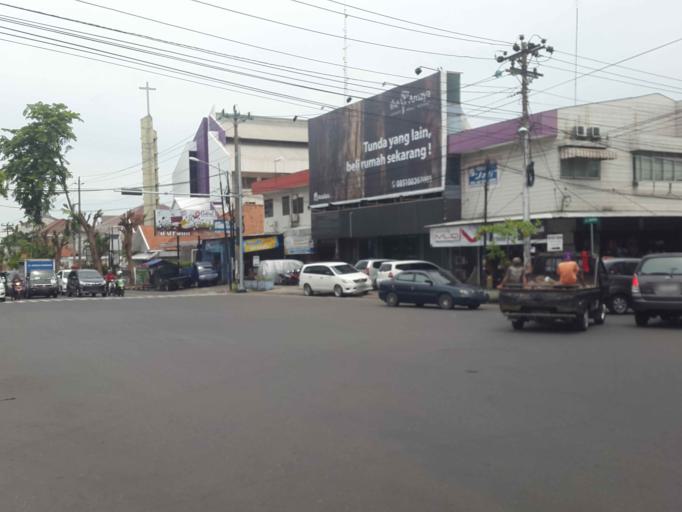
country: ID
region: Central Java
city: Semarang
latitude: -7.0011
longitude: 110.4333
